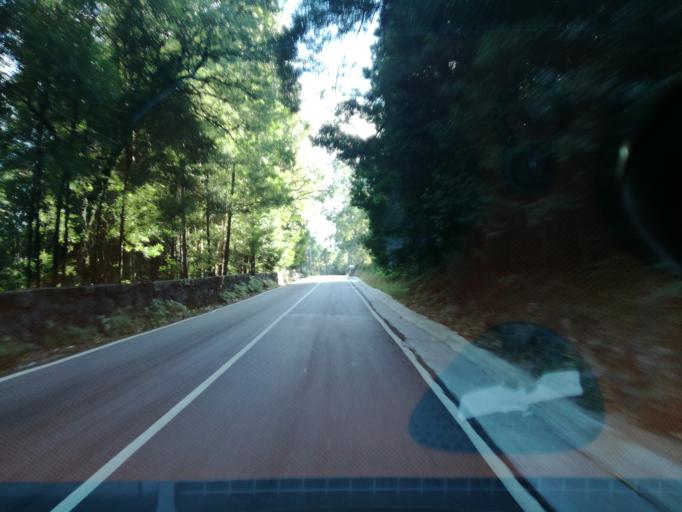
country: PT
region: Porto
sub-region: Santo Tirso
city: Sao Miguel do Couto
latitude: 41.3093
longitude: -8.4451
